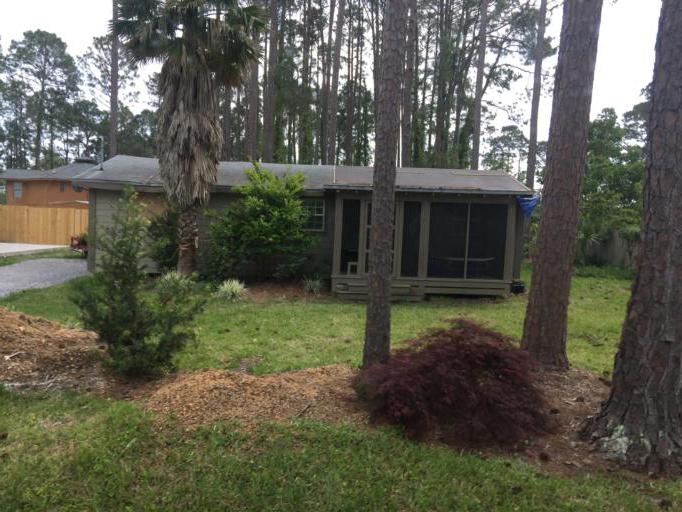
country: US
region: Florida
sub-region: Bay County
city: Laguna Beach
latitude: 30.2355
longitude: -85.8888
